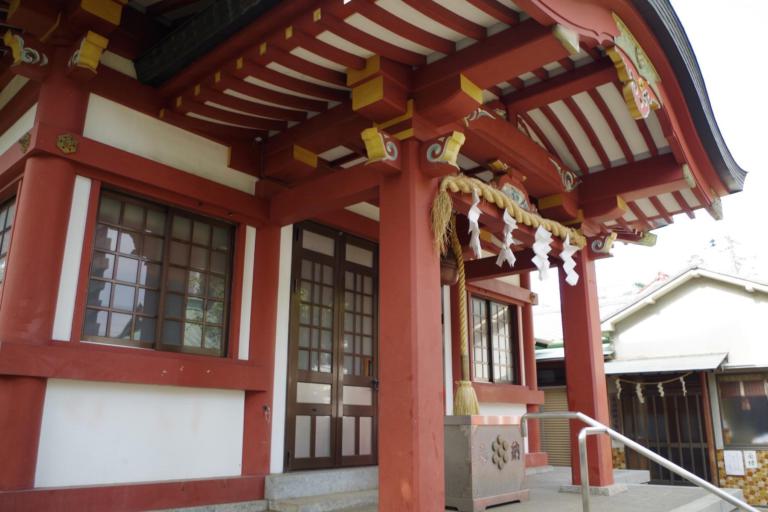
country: JP
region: Tokyo
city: Urayasu
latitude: 35.7235
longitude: 139.8228
